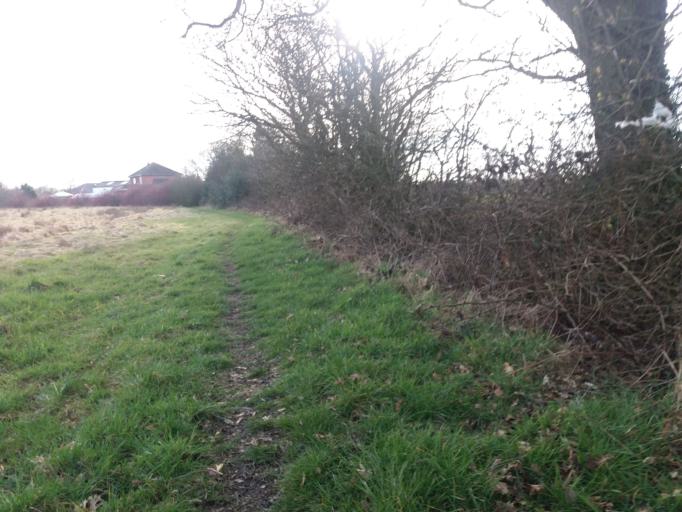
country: GB
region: England
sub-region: Lancashire
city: Euxton
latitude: 53.6474
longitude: -2.6752
